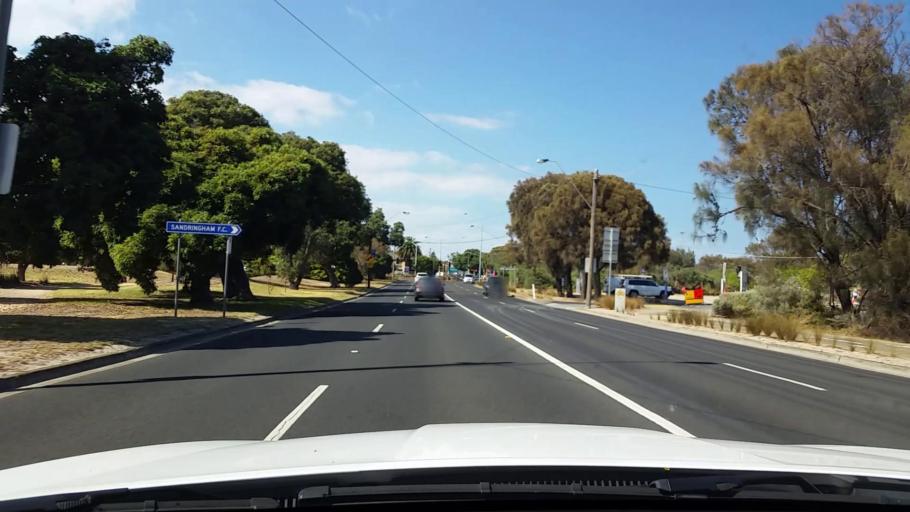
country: AU
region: Victoria
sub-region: Bayside
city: Hampton
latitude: -37.9422
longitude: 145.0004
